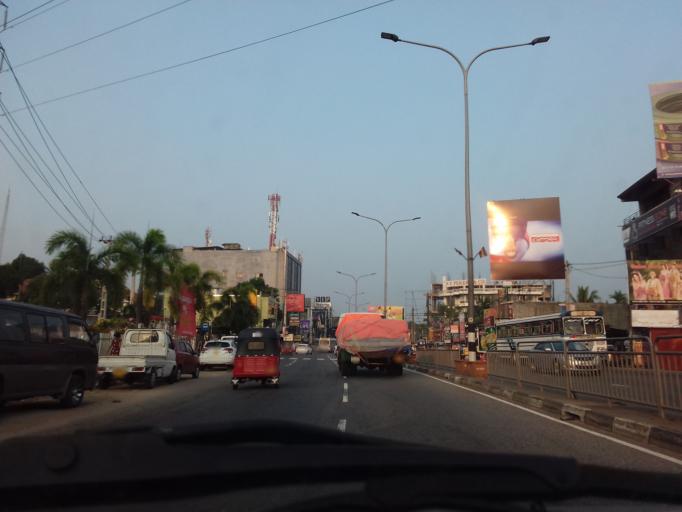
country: LK
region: Western
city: Kelaniya
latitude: 6.9717
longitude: 79.9166
